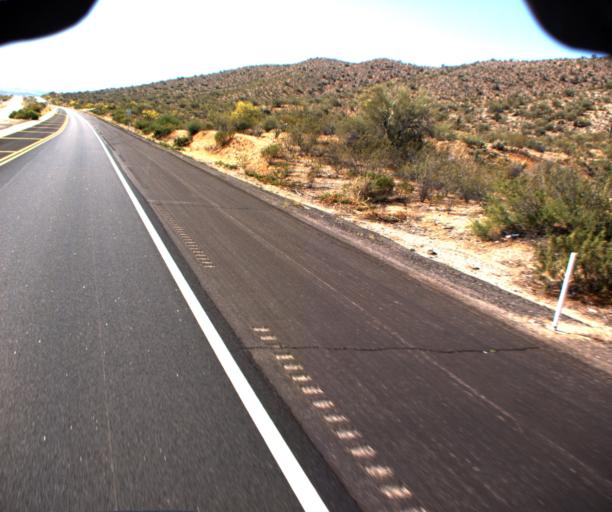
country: US
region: Arizona
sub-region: Yavapai County
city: Bagdad
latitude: 34.6894
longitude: -113.6033
